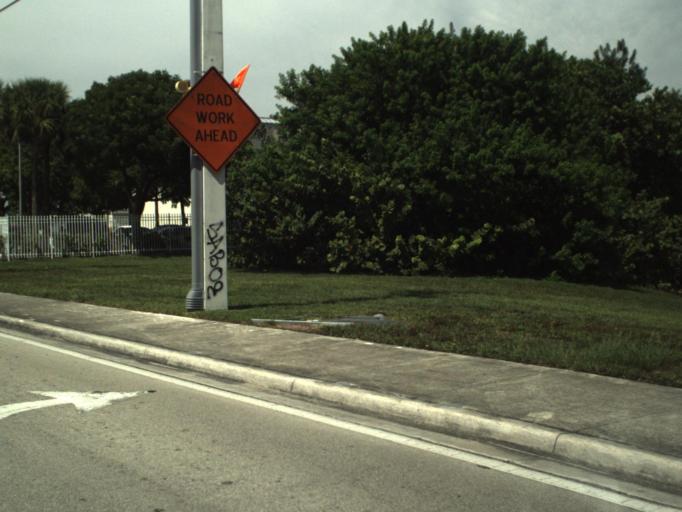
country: US
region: Florida
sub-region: Broward County
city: Dania Beach
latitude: 26.0614
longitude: -80.1684
